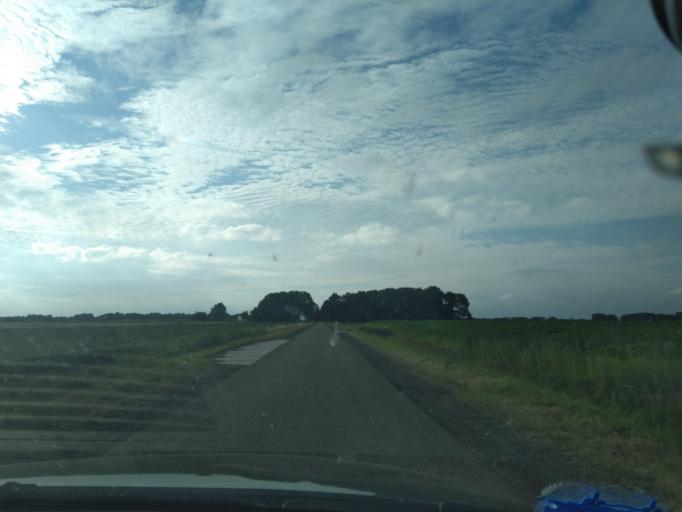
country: NL
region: Groningen
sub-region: Gemeente Vlagtwedde
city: Vlagtwedde
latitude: 53.0869
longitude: 7.1040
